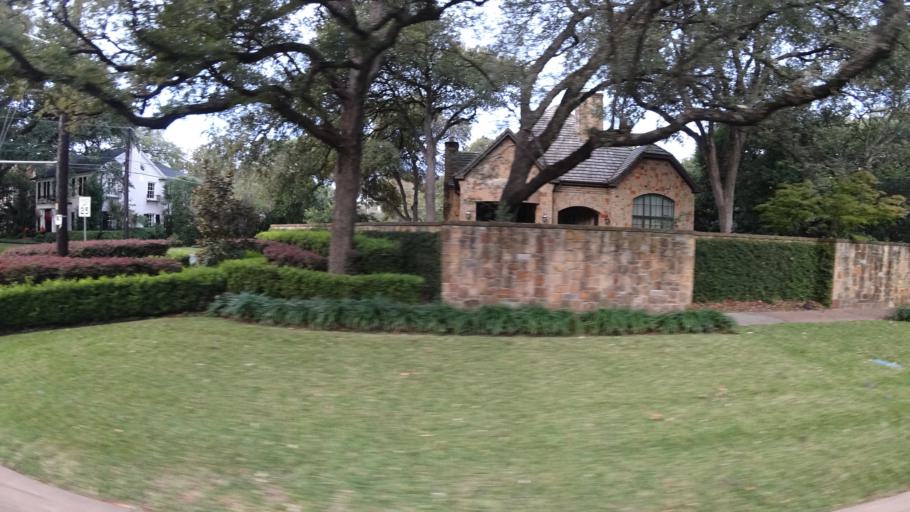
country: US
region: Texas
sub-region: Travis County
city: Austin
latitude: 30.2930
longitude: -97.7562
